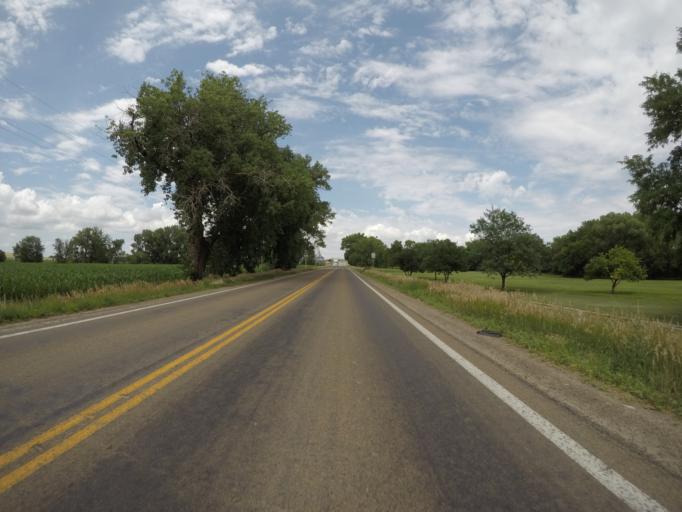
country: US
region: Kansas
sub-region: Rawlins County
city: Atwood
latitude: 39.8181
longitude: -101.0468
